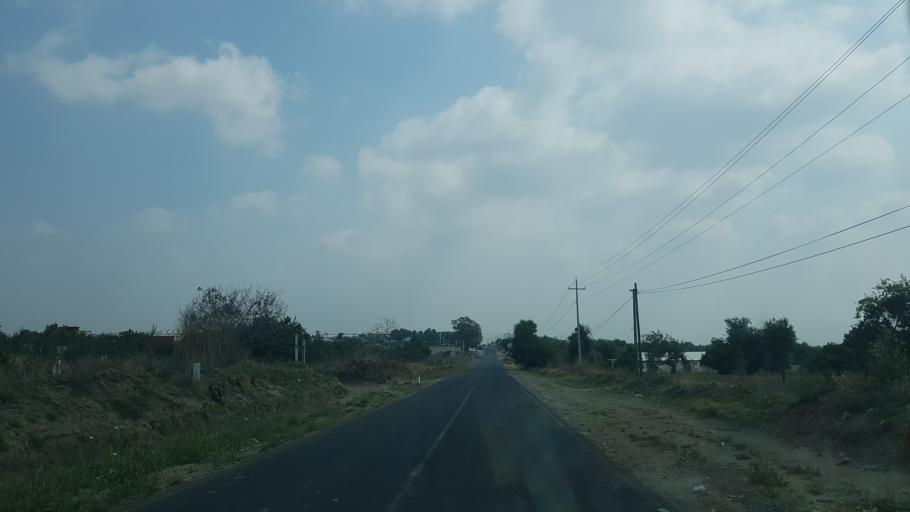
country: MX
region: Puebla
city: Huejotzingo
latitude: 19.1337
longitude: -98.4154
